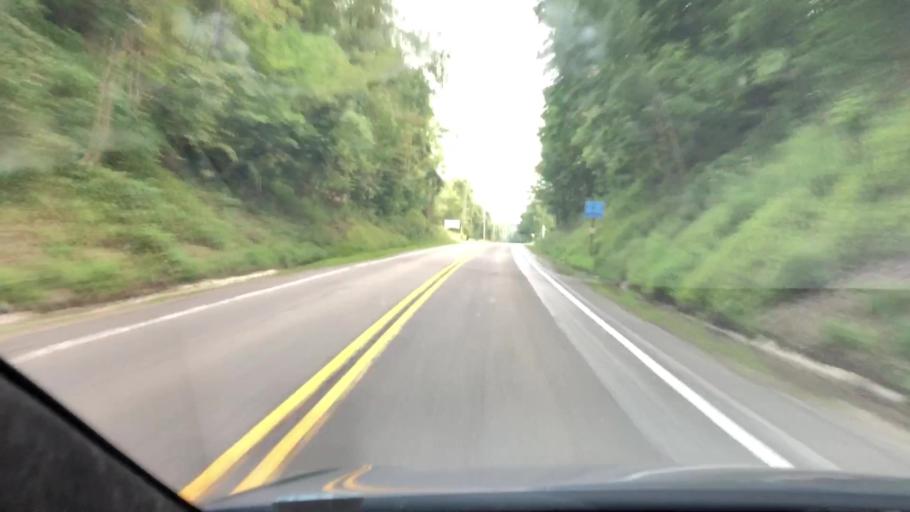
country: US
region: Pennsylvania
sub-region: Butler County
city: Slippery Rock
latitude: 41.0895
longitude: -80.0018
